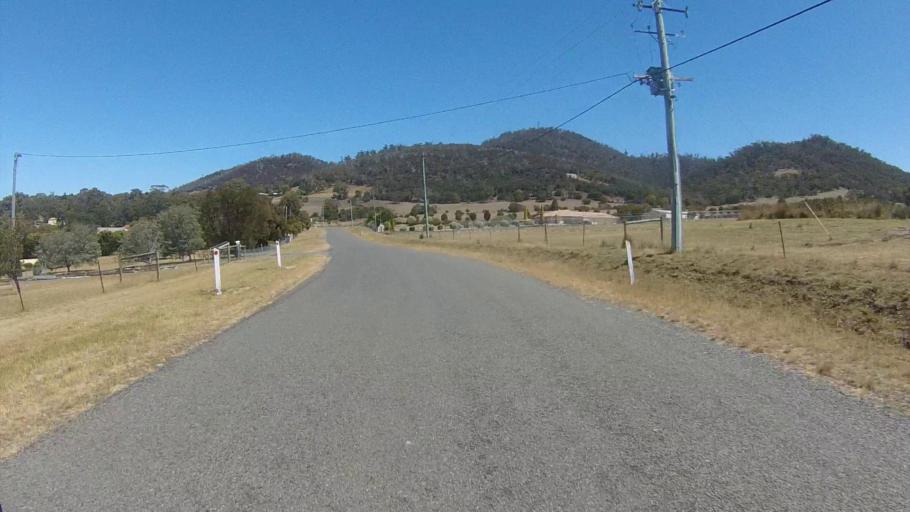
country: AU
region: Tasmania
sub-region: Clarence
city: Cambridge
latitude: -42.8479
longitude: 147.4637
